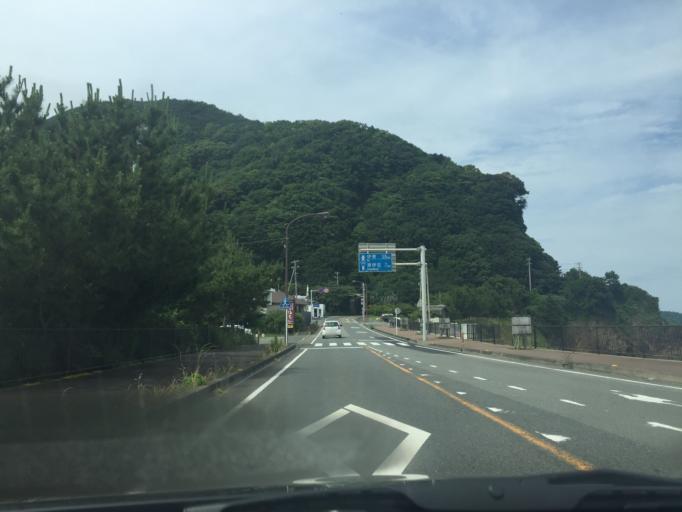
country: JP
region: Shizuoka
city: Shimoda
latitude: 34.7456
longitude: 138.9994
